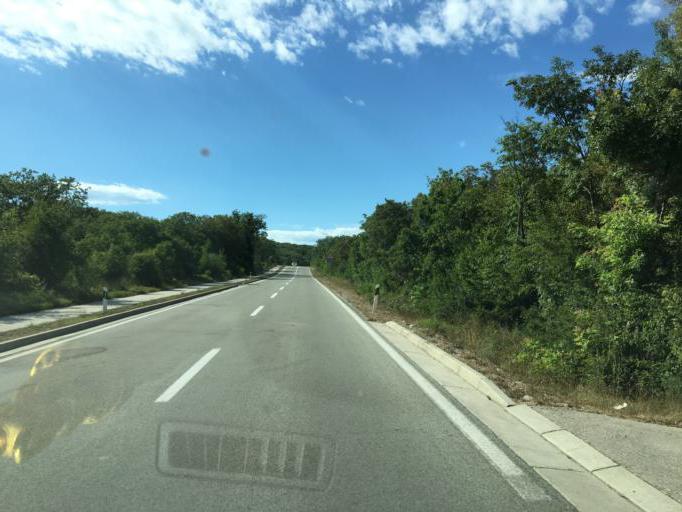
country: HR
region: Primorsko-Goranska
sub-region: Grad Krk
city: Krk
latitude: 45.0710
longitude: 14.5532
